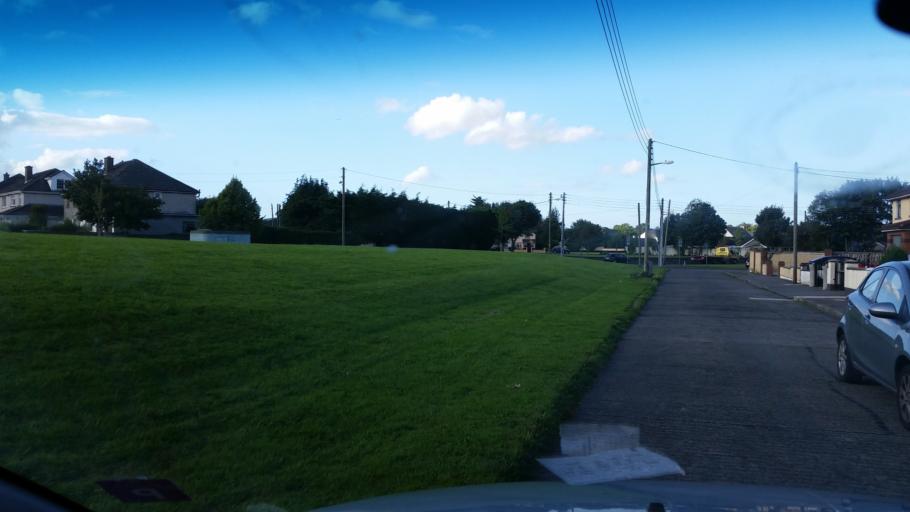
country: IE
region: Leinster
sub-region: Fingal County
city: Blanchardstown
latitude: 53.3833
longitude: -6.3773
